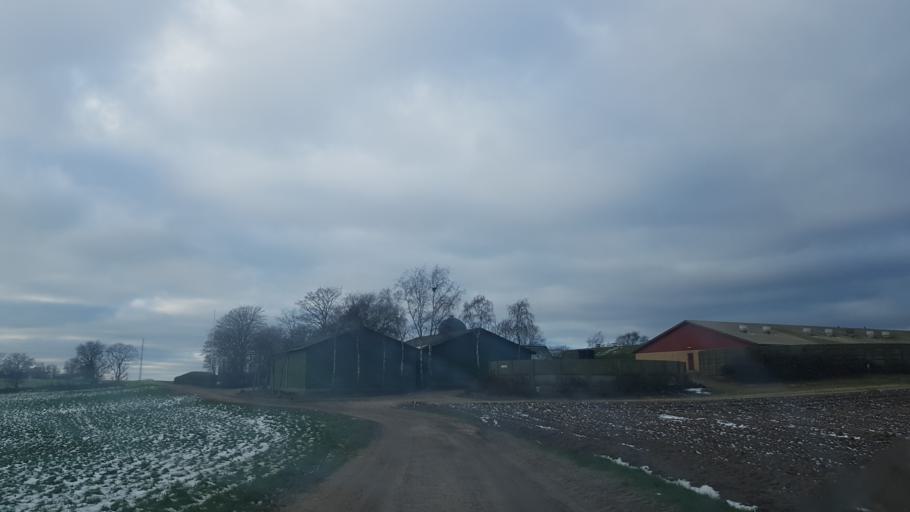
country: DK
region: Zealand
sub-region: Odsherred Kommune
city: Hojby
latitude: 55.9243
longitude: 11.5718
